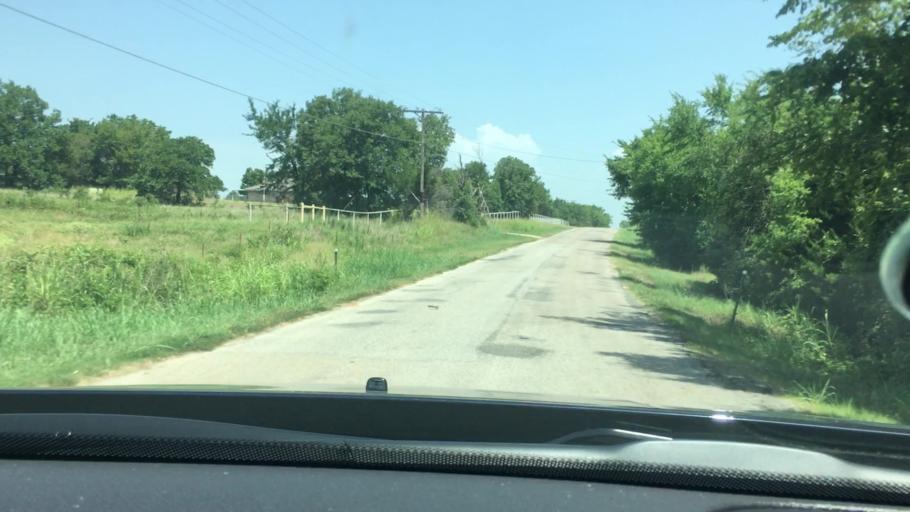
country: US
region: Oklahoma
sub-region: Pontotoc County
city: Byng
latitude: 34.8284
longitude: -96.6698
